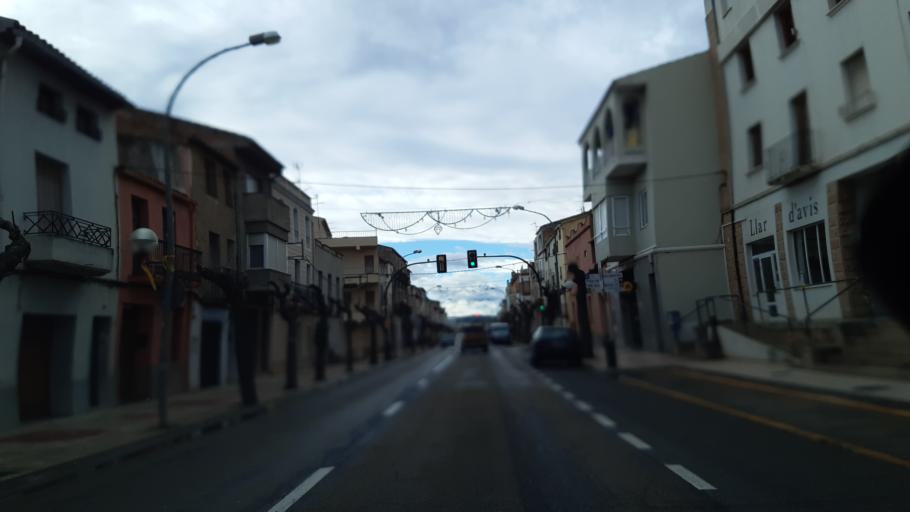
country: ES
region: Catalonia
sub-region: Provincia de Tarragona
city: Gandesa
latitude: 41.0768
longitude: 0.4757
